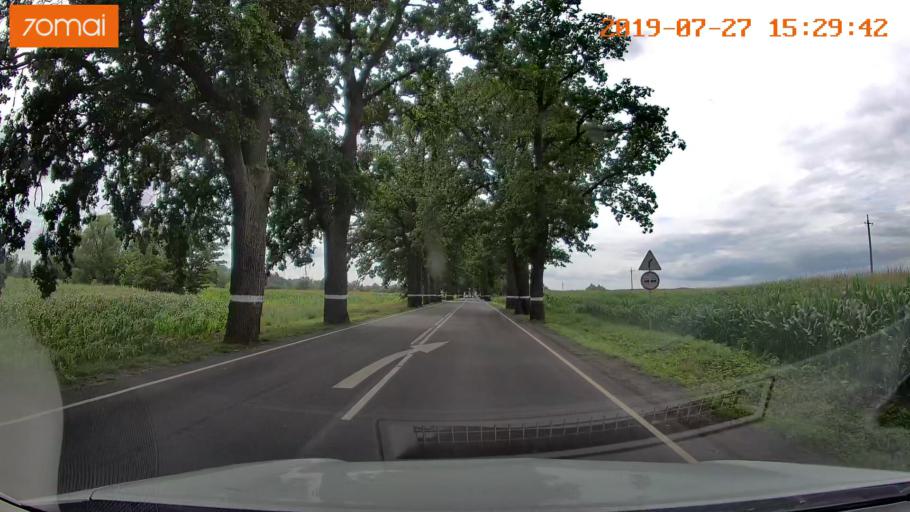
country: RU
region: Kaliningrad
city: Nesterov
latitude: 54.6311
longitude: 22.5255
